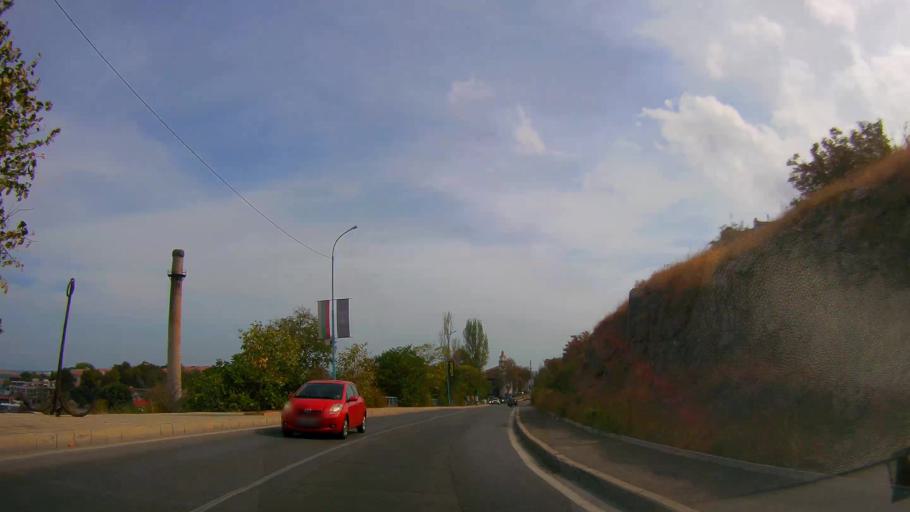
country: BG
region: Burgas
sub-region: Obshtina Sozopol
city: Sozopol
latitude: 42.4183
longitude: 27.6915
